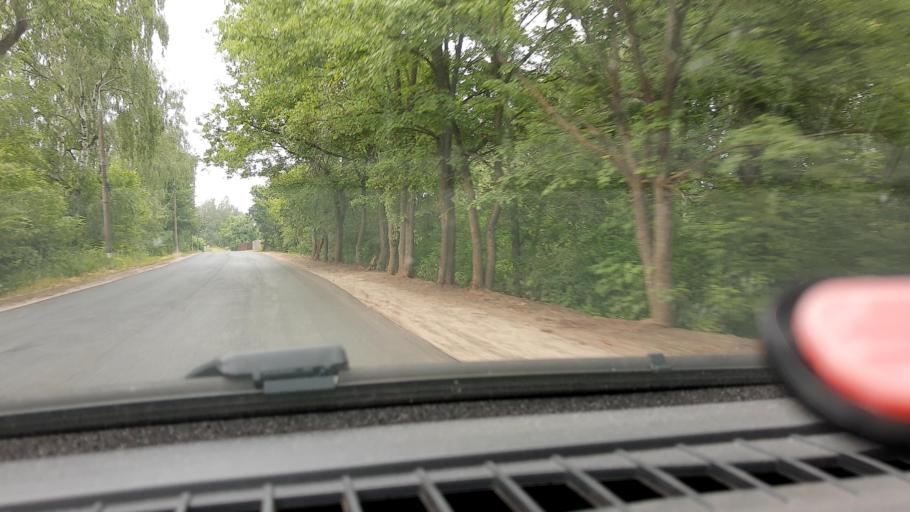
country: RU
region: Nizjnij Novgorod
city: Gorodets
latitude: 56.6321
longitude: 43.4771
